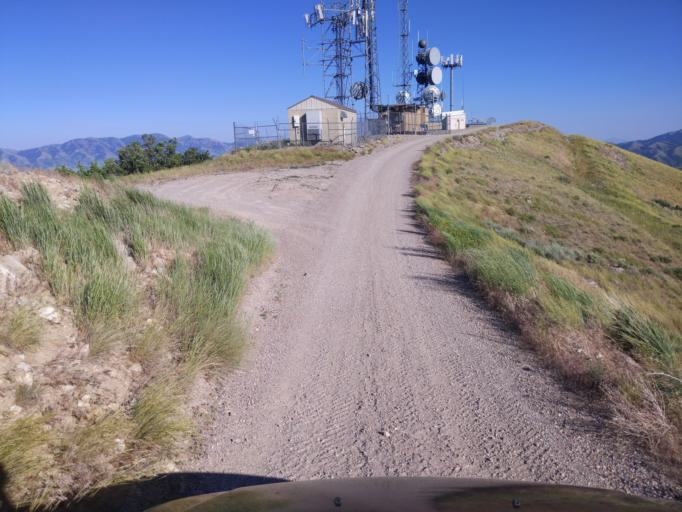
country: US
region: Idaho
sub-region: Bannock County
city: Pocatello
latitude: 42.8482
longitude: -112.3623
